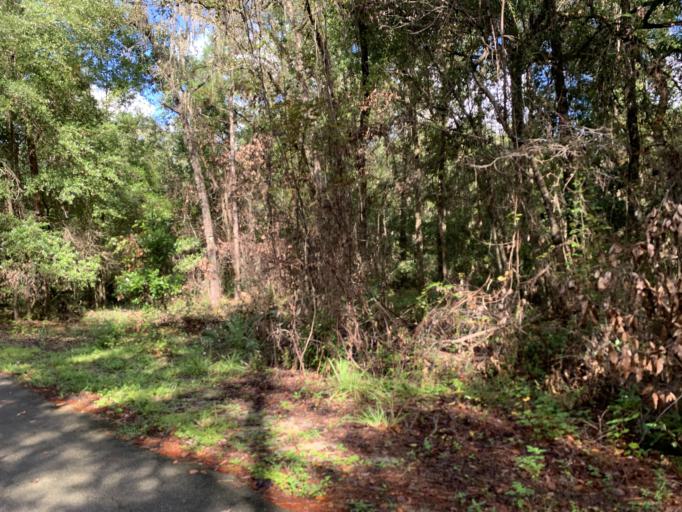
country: US
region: Florida
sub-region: Marion County
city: Silver Springs Shores
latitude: 29.1558
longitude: -82.0402
